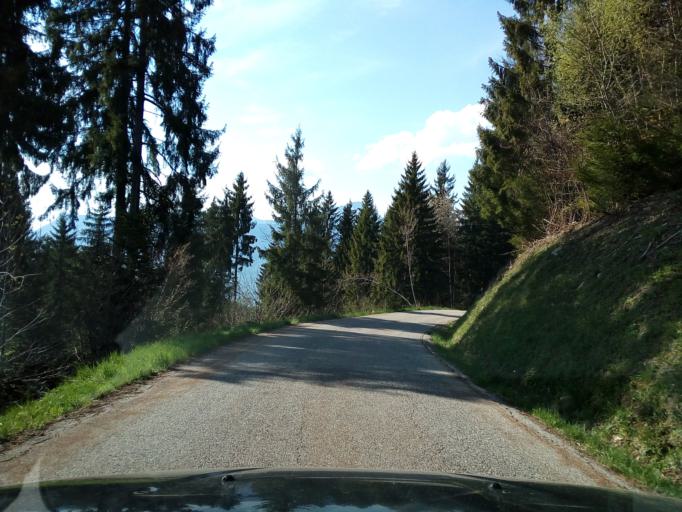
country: FR
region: Rhone-Alpes
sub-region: Departement de l'Isere
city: Revel
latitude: 45.1938
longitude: 5.8916
